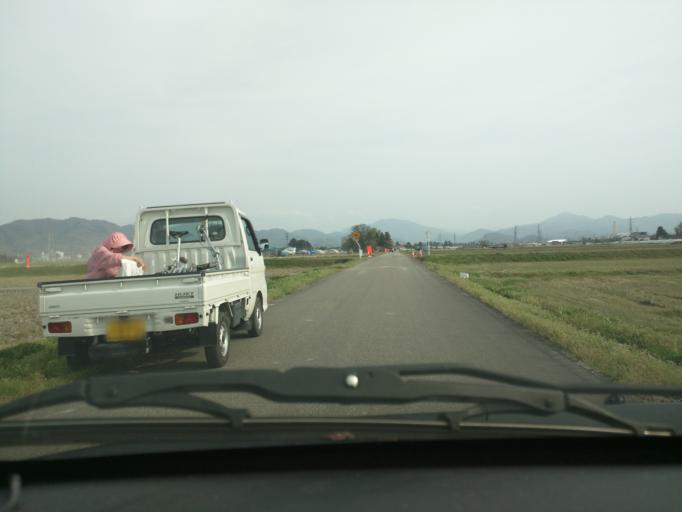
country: JP
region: Fukushima
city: Kitakata
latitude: 37.5106
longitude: 139.8961
